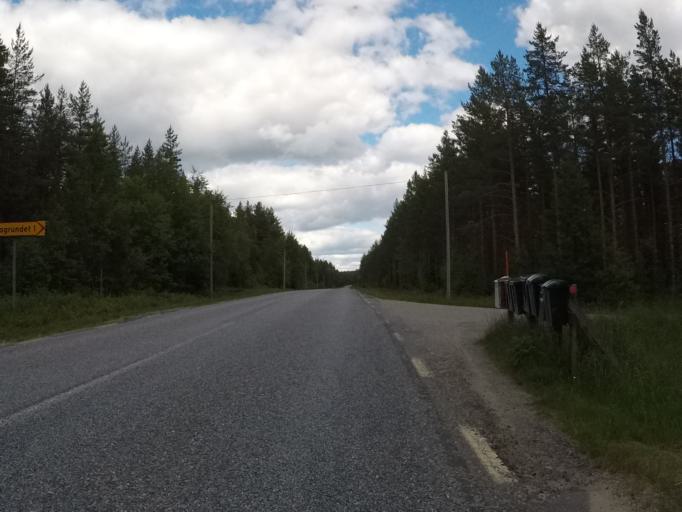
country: SE
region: Vaesterbotten
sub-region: Umea Kommun
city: Saevar
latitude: 63.9458
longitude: 20.7902
